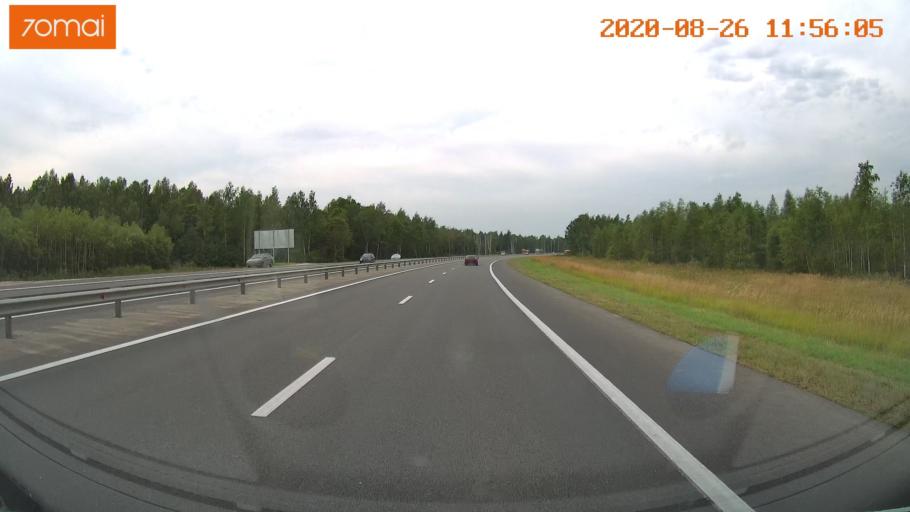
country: RU
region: Rjazan
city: Kiritsy
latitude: 54.2649
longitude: 40.3861
